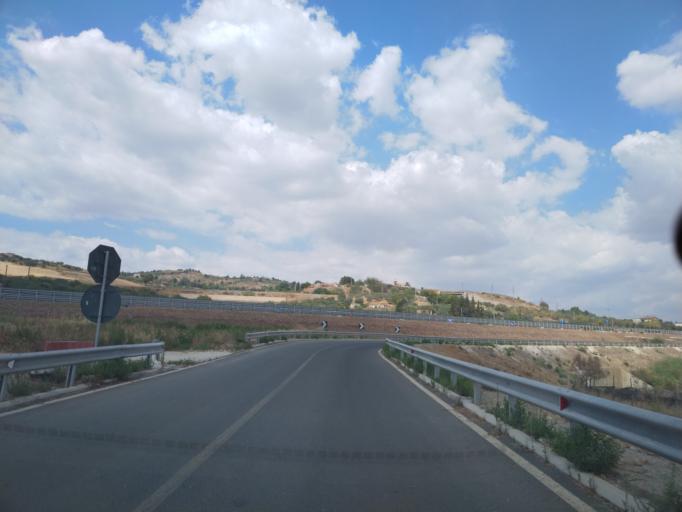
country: IT
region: Sicily
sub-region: Provincia di Caltanissetta
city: San Cataldo
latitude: 37.4509
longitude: 13.9743
